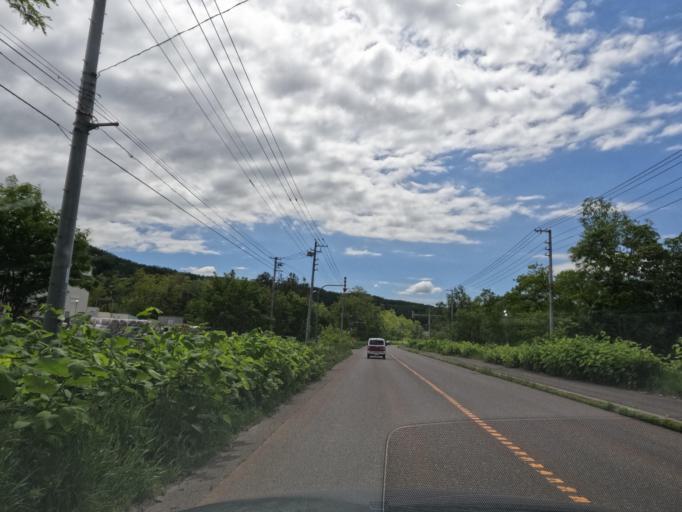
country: JP
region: Hokkaido
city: Bibai
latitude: 43.2491
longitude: 141.9103
